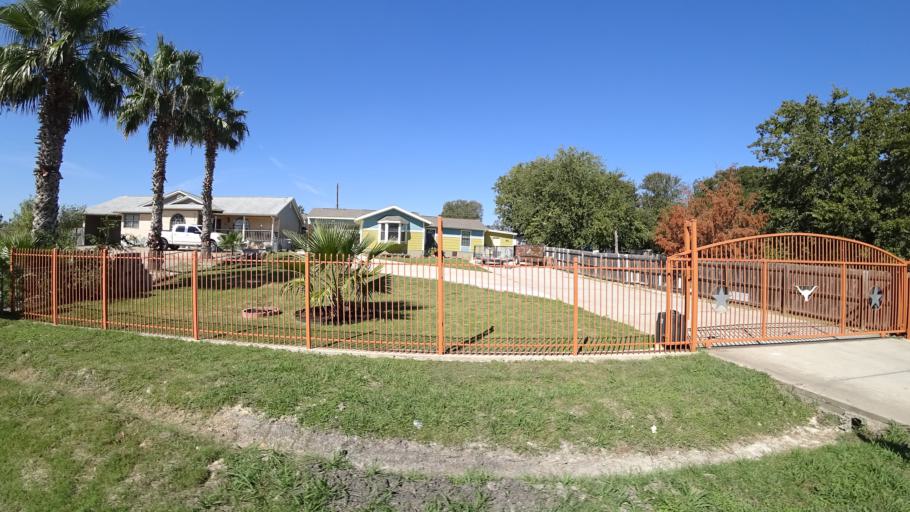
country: US
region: Texas
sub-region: Travis County
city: Hornsby Bend
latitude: 30.2781
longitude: -97.6220
